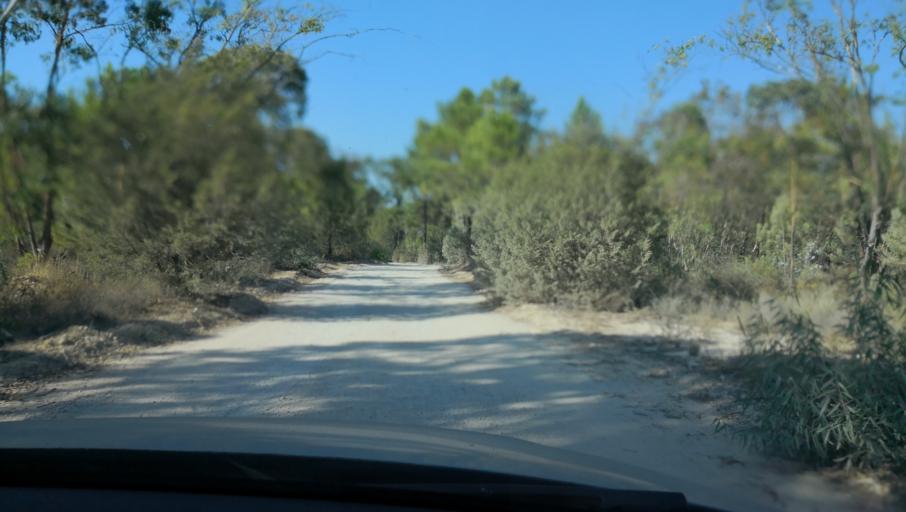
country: PT
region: Setubal
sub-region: Setubal
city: Setubal
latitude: 38.4768
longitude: -8.8799
